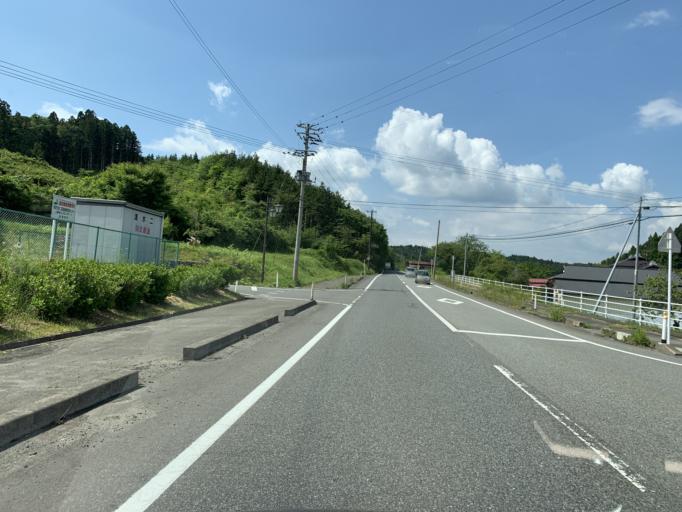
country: JP
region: Miyagi
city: Furukawa
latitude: 38.7280
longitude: 140.9533
